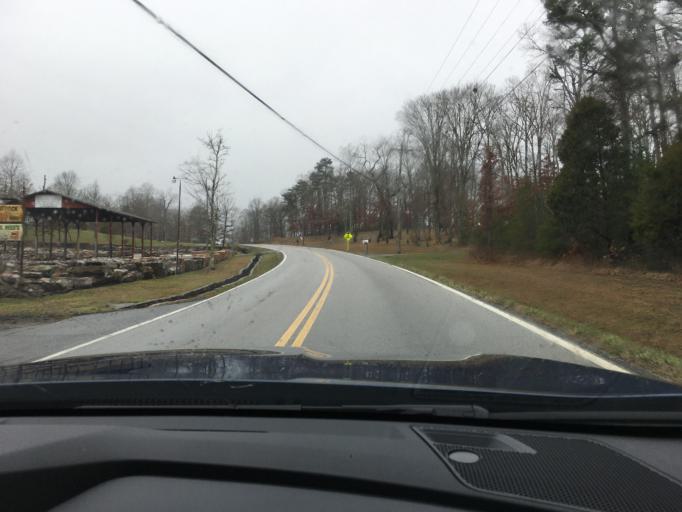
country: US
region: Tennessee
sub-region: Rhea County
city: Spring City
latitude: 35.7638
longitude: -84.8640
